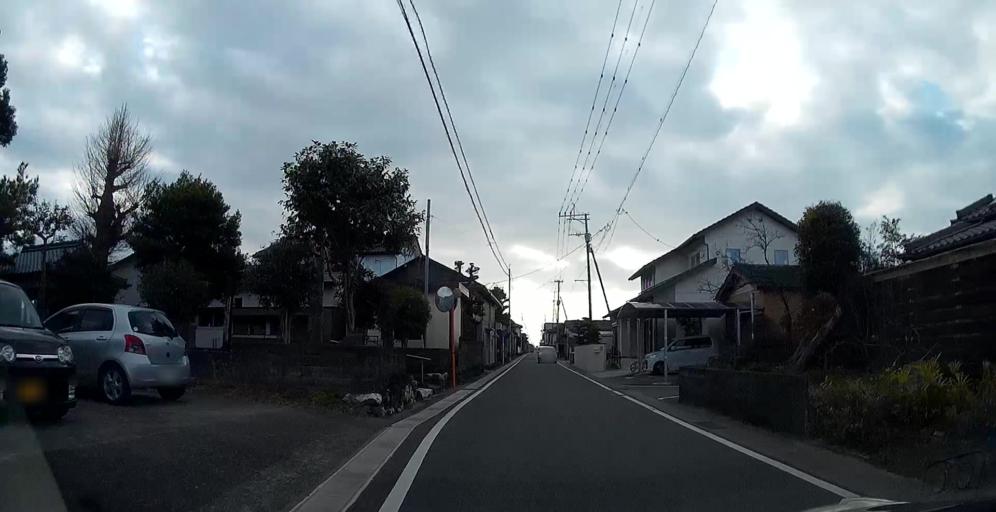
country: JP
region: Kumamoto
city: Yatsushiro
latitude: 32.5503
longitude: 130.6186
